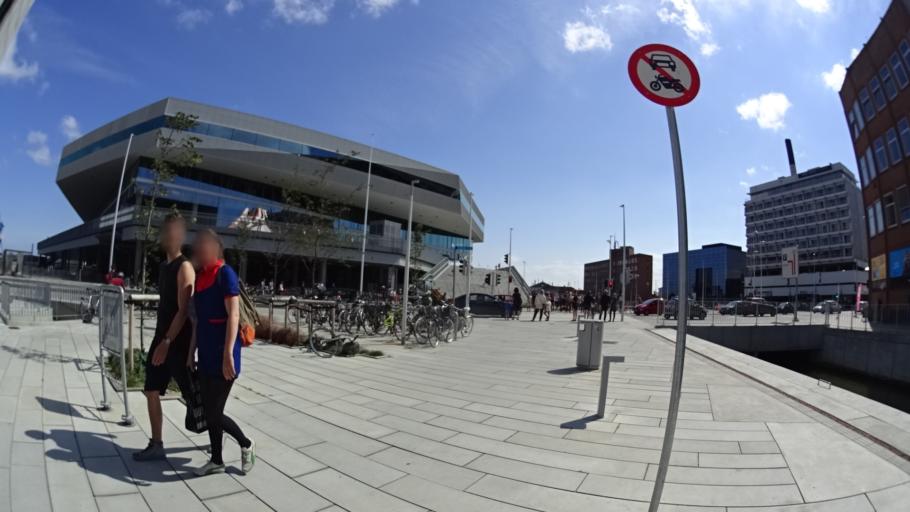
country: DK
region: Central Jutland
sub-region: Arhus Kommune
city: Arhus
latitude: 56.1538
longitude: 10.2122
